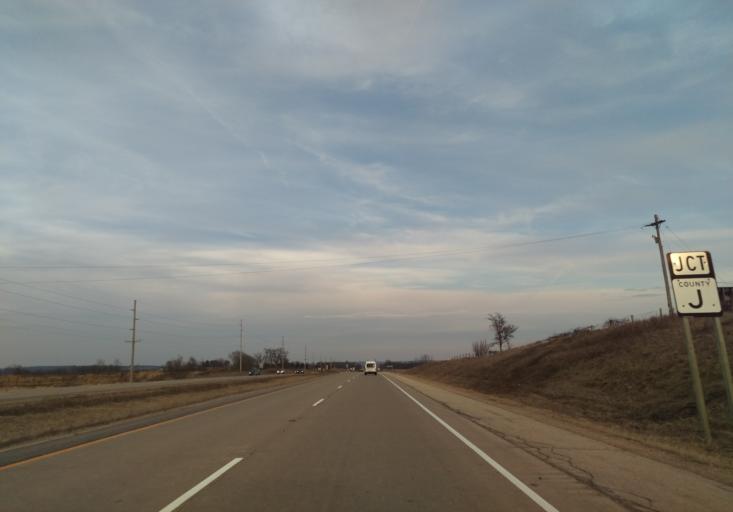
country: US
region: Wisconsin
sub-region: Dane County
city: Verona
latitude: 42.9878
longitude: -89.6364
